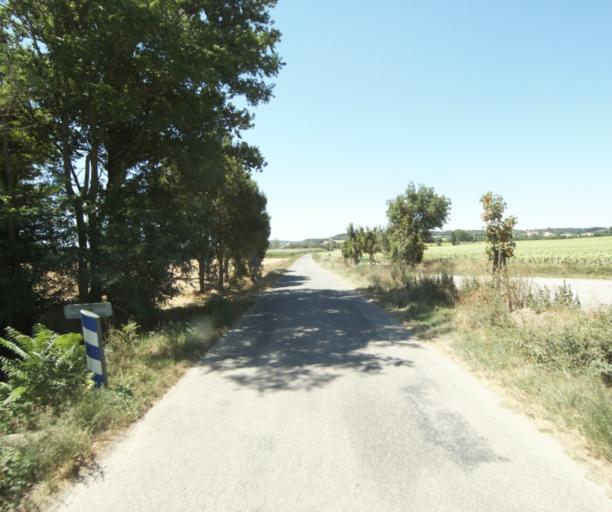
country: FR
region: Midi-Pyrenees
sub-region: Departement de la Haute-Garonne
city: Saint-Felix-Lauragais
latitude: 43.4640
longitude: 1.9454
